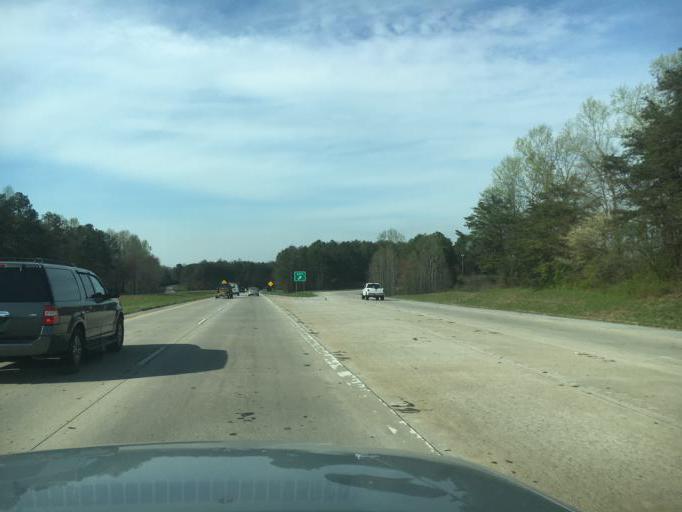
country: US
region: Georgia
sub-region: Habersham County
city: Cornelia
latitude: 34.5329
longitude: -83.5406
